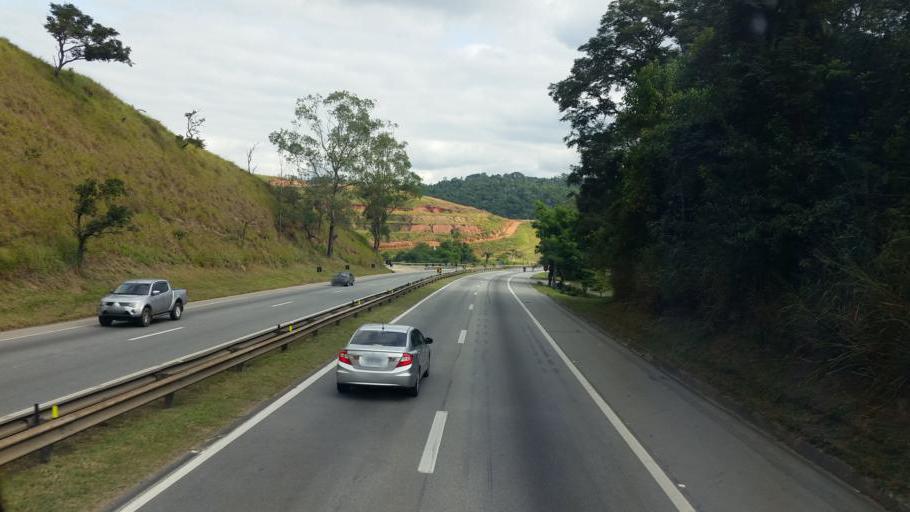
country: BR
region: Sao Paulo
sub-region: Santa Isabel
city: Santa Isabel
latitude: -23.3549
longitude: -46.2039
